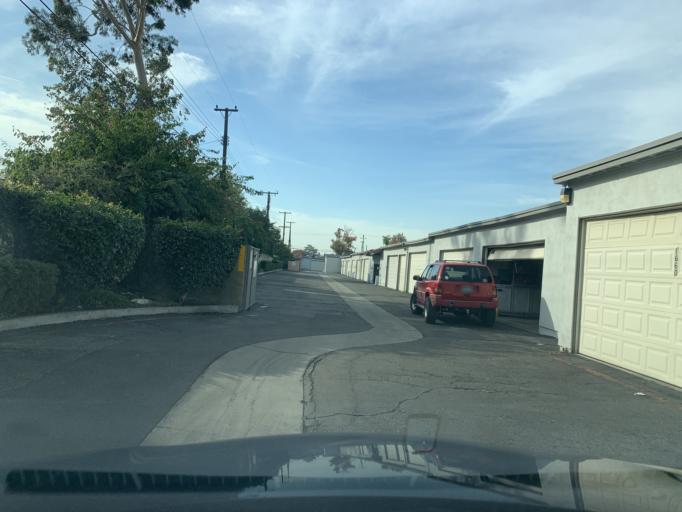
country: US
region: California
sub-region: Orange County
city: Garden Grove
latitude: 33.7933
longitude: -117.9394
